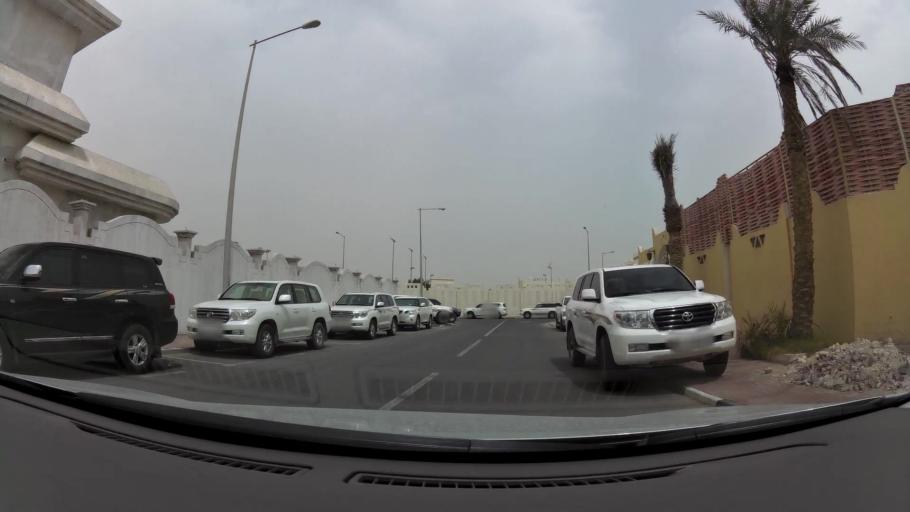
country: QA
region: Baladiyat ad Dawhah
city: Doha
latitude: 25.2588
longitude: 51.5086
